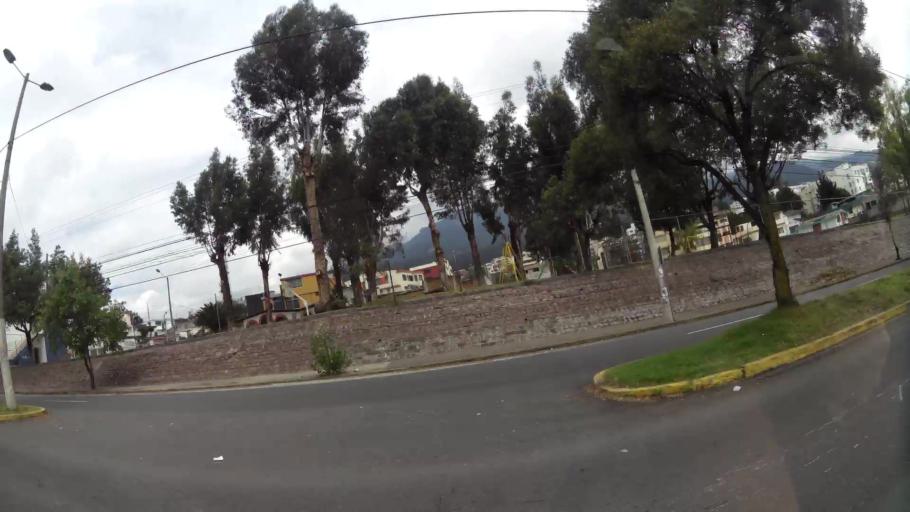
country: EC
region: Pichincha
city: Quito
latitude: -0.1583
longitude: -78.4906
